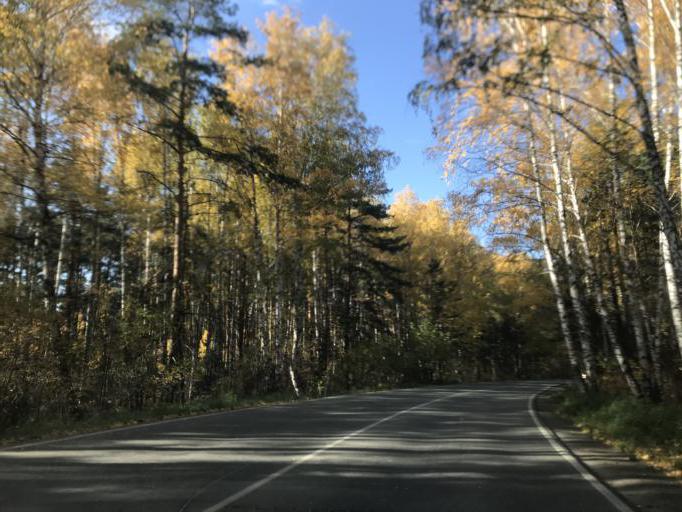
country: RU
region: Chelyabinsk
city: Dolgoderevenskoye
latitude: 55.2840
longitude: 61.3598
